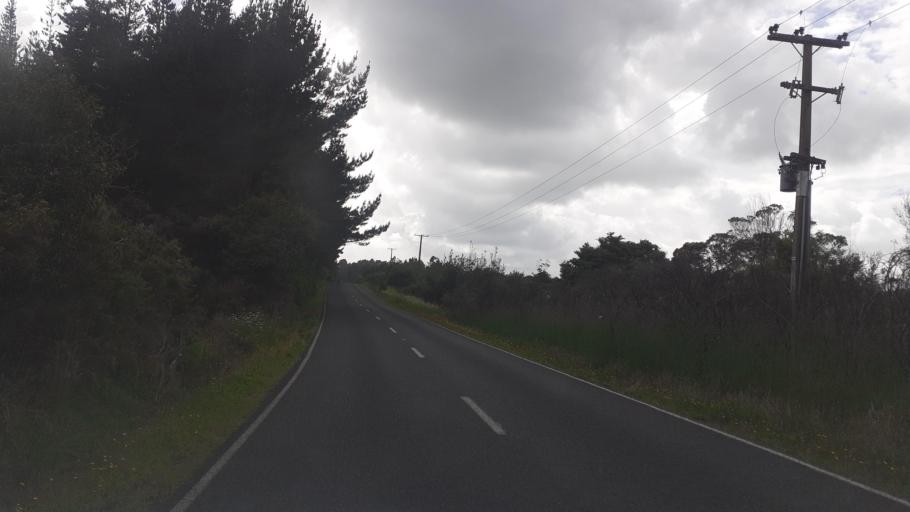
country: NZ
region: Northland
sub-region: Far North District
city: Kerikeri
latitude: -35.2256
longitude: 174.0153
